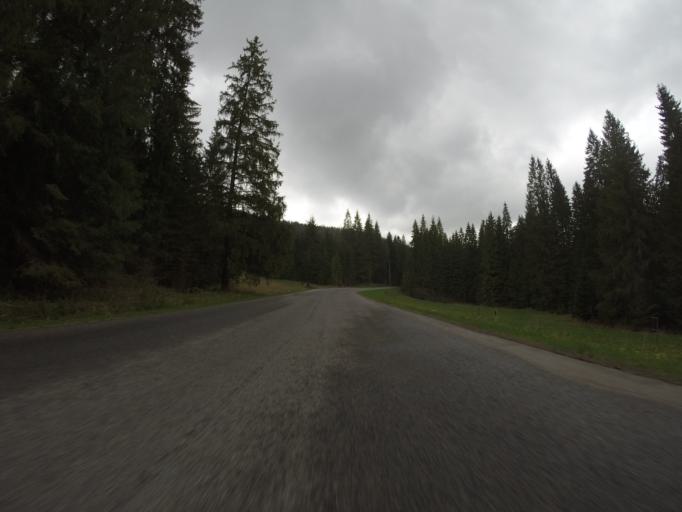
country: SK
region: Banskobystricky
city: Revuca
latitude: 48.8073
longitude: 20.1426
